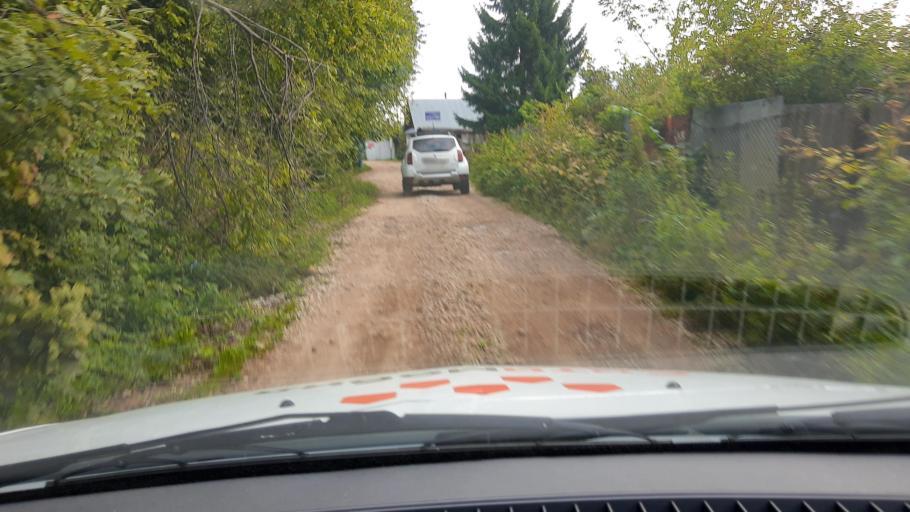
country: RU
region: Bashkortostan
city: Kabakovo
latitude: 54.7098
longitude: 56.1389
